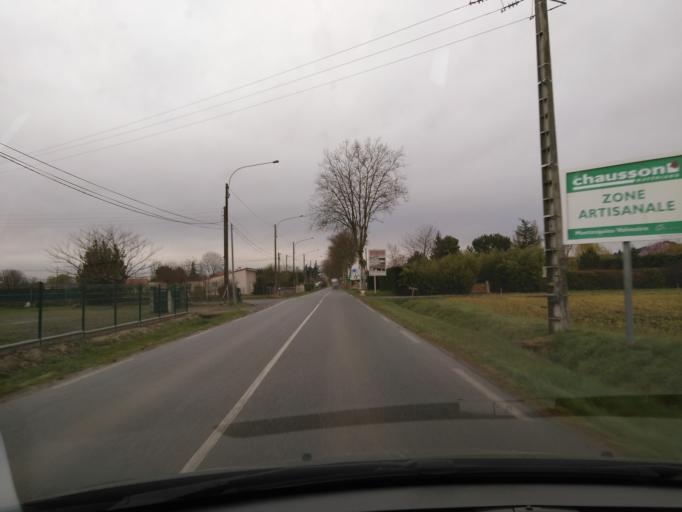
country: FR
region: Midi-Pyrenees
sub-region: Departement de la Haute-Garonne
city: Montesquieu-Volvestre
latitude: 43.1952
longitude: 1.2335
